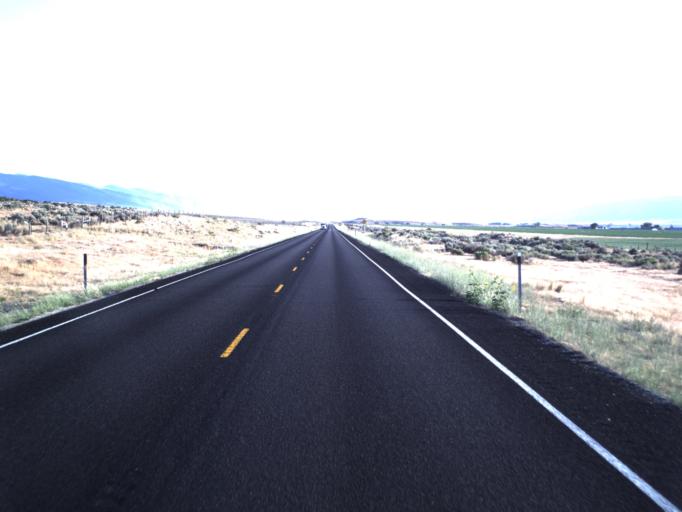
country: US
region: Utah
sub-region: Sanpete County
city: Ephraim
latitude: 39.4377
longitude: -111.5505
